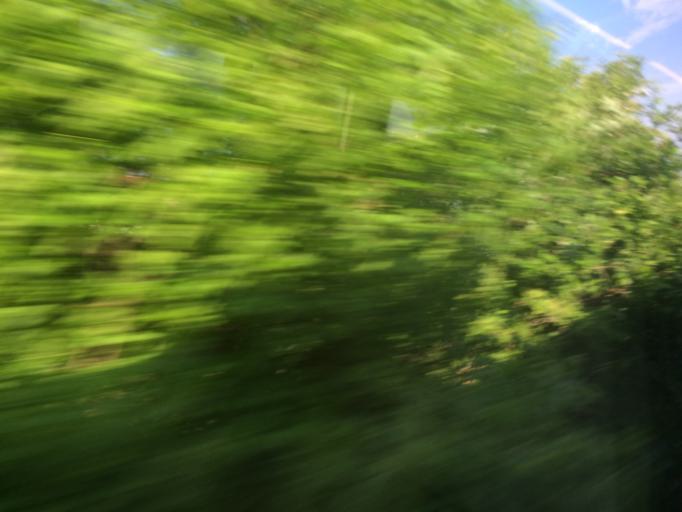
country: GB
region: Scotland
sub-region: Stirling
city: Bridge of Allan
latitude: 56.1381
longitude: -3.9396
